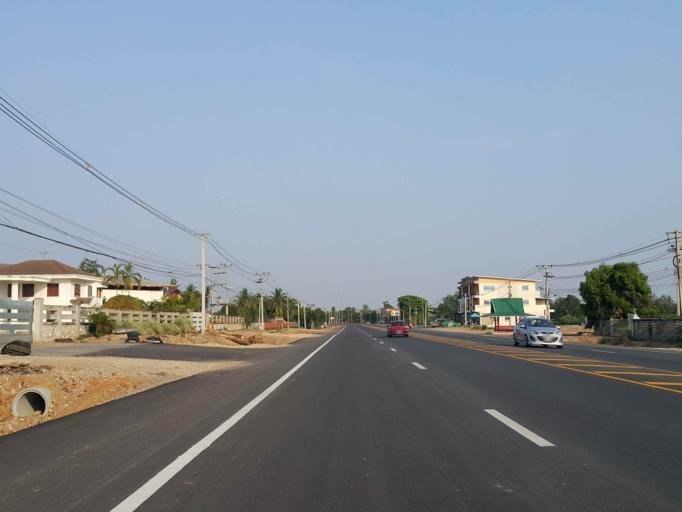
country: TH
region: Sukhothai
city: Sawankhalok
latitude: 17.3055
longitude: 99.8205
